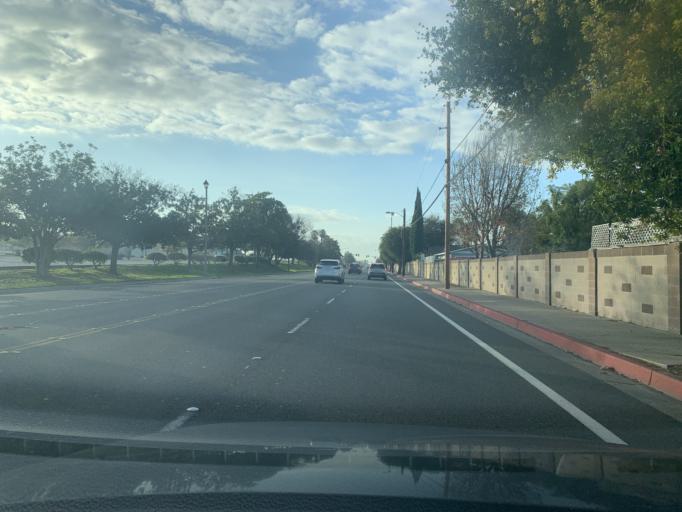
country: US
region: California
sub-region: Orange County
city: Westminster
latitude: 33.7489
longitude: -118.0159
